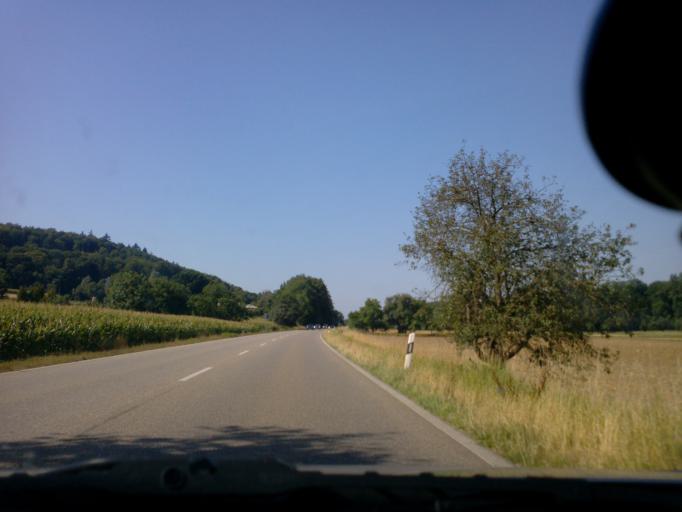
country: DE
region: Baden-Wuerttemberg
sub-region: Karlsruhe Region
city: Weingarten
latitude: 49.0359
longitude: 8.5196
